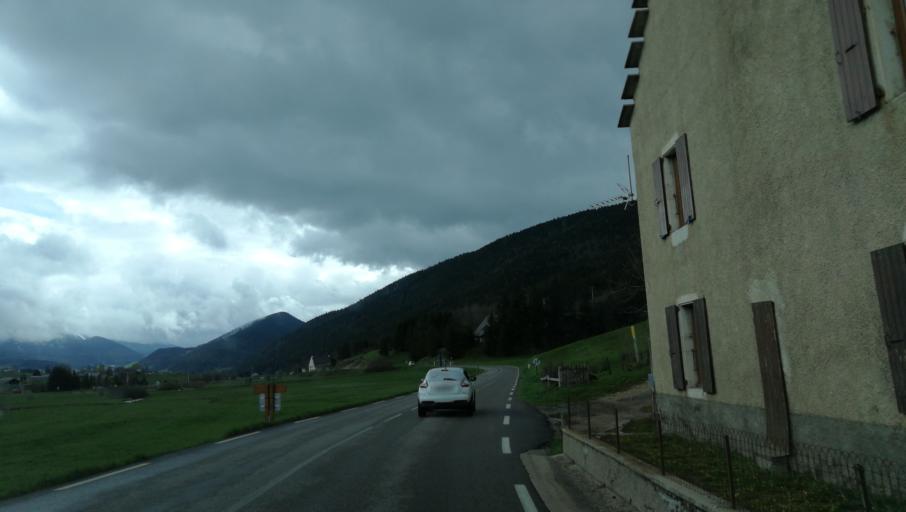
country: FR
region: Rhone-Alpes
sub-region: Departement de l'Isere
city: Villard-de-Lans
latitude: 45.1006
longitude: 5.5599
